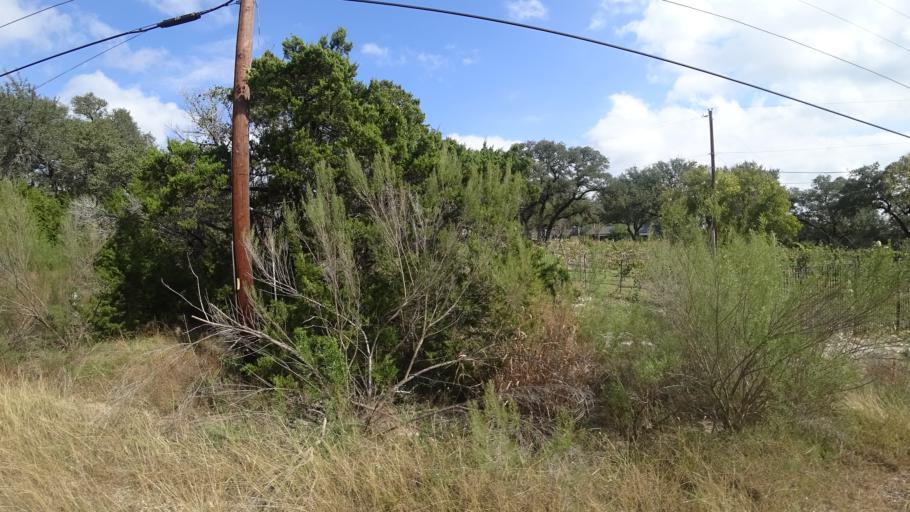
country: US
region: Texas
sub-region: Travis County
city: Barton Creek
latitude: 30.3030
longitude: -97.8733
